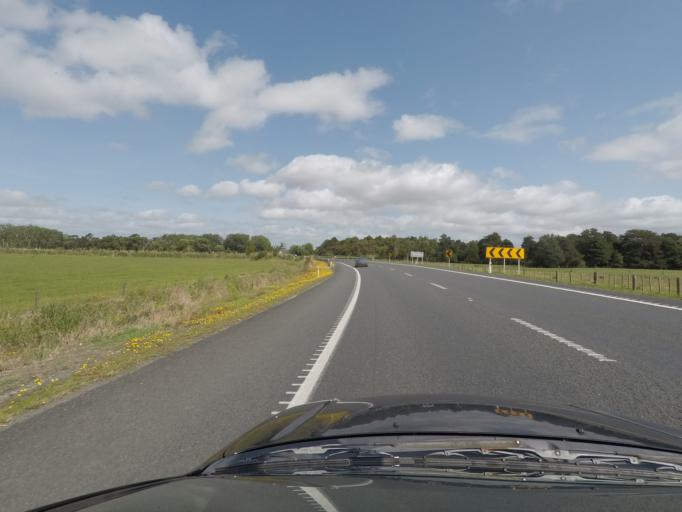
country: NZ
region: Northland
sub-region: Whangarei
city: Ruakaka
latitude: -35.8598
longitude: 174.3906
